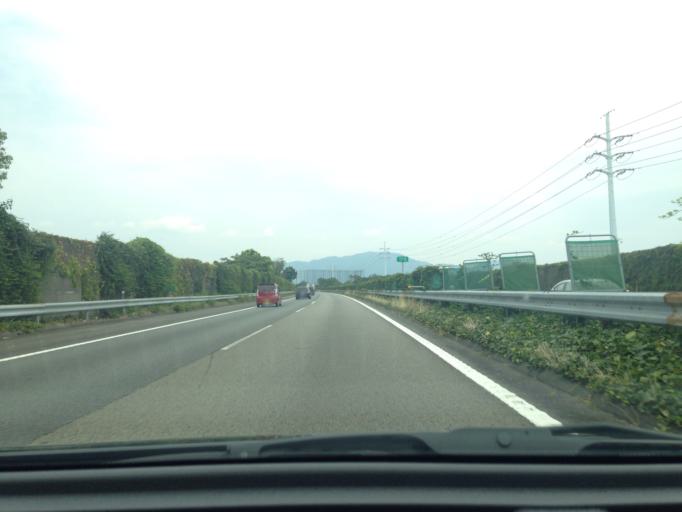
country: JP
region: Shizuoka
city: Fujieda
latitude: 34.8366
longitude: 138.2799
